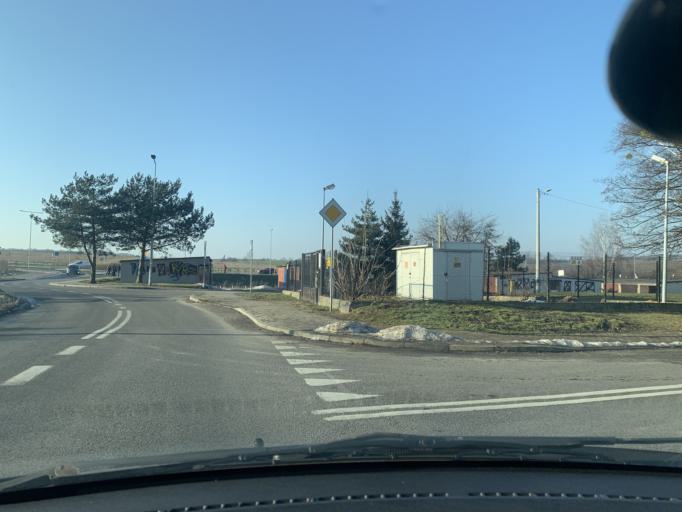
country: PL
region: Silesian Voivodeship
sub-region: Powiat tarnogorski
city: Radzionkow
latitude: 50.4054
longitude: 18.8946
